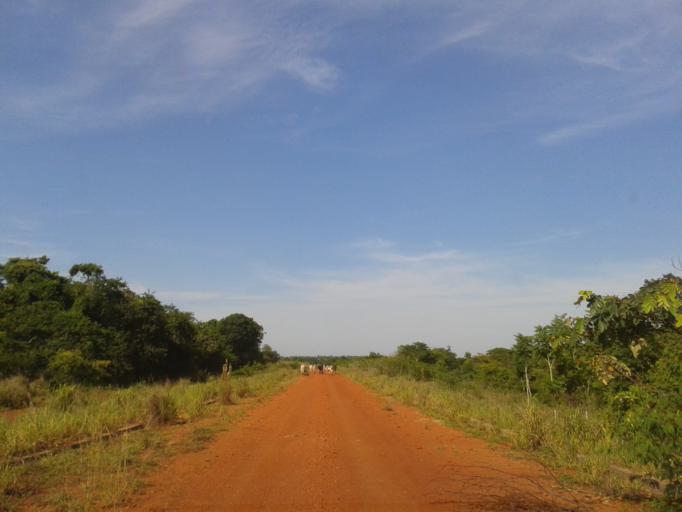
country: BR
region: Minas Gerais
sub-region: Santa Vitoria
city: Santa Vitoria
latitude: -19.1154
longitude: -50.5479
